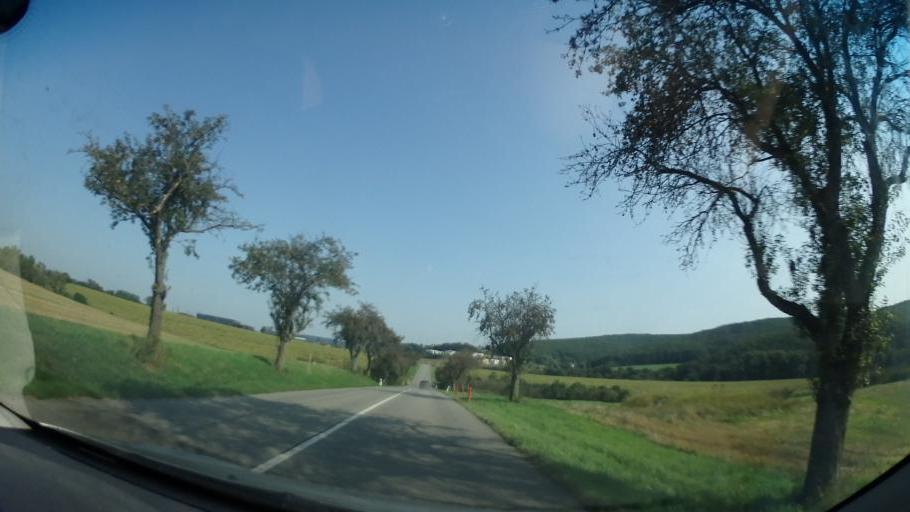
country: CZ
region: South Moravian
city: Kurim
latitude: 49.2562
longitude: 16.5256
